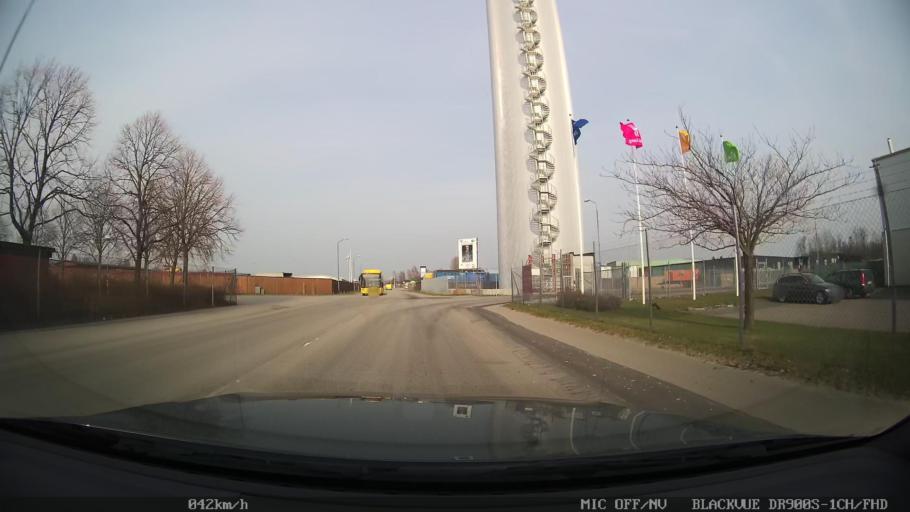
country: SE
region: Skane
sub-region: Ystads Kommun
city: Ystad
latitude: 55.4410
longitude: 13.8417
